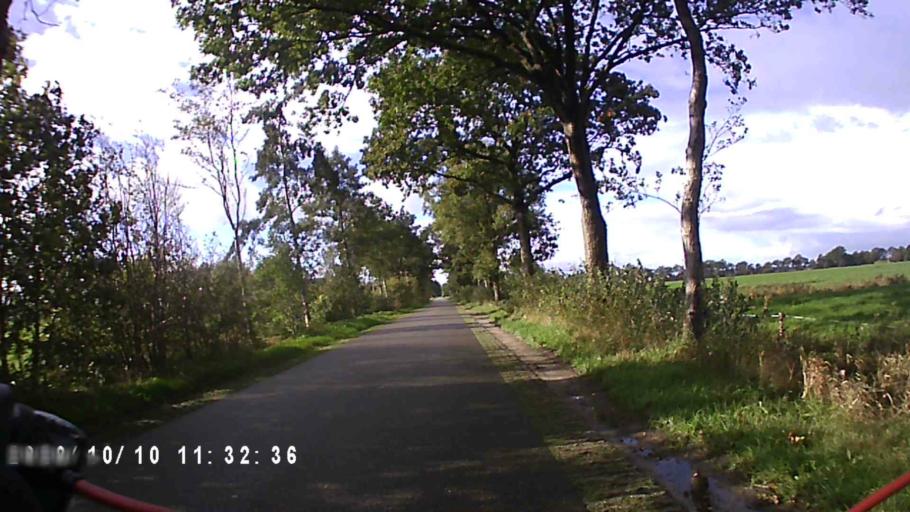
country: NL
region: Friesland
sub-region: Gemeente Smallingerland
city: Drachten
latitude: 53.0821
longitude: 6.1334
